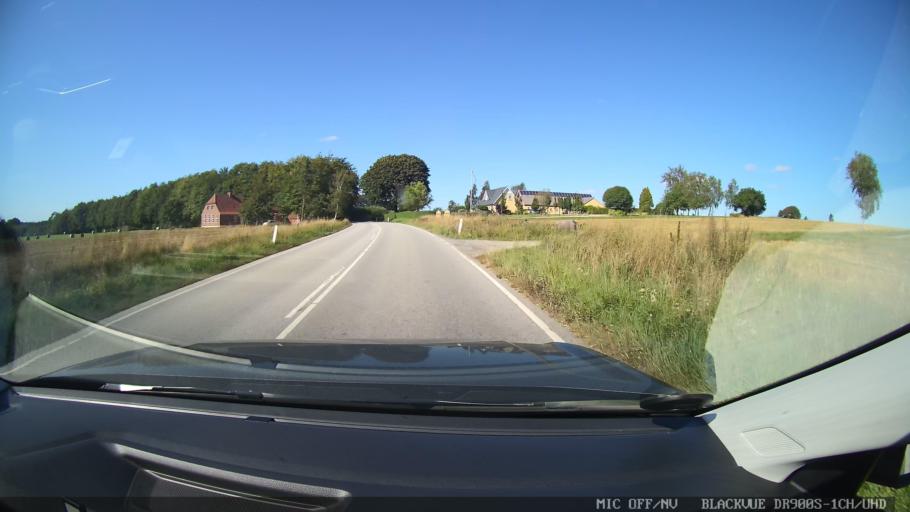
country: DK
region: North Denmark
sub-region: Mariagerfjord Kommune
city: Mariager
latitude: 56.6126
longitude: 9.9895
